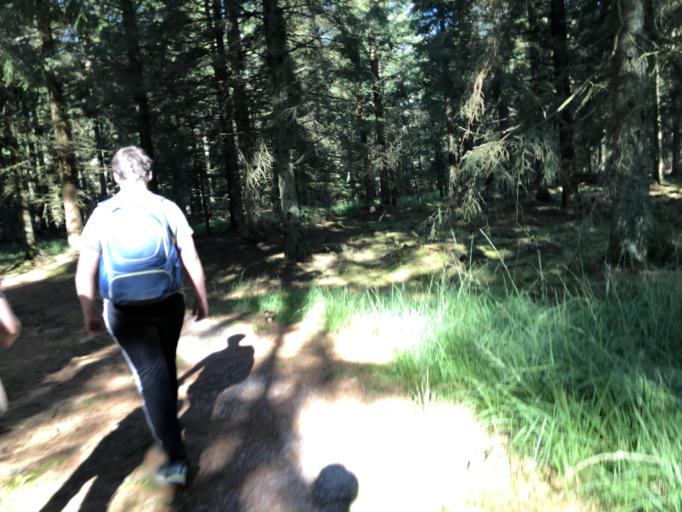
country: DK
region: Central Jutland
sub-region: Lemvig Kommune
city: Lemvig
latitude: 56.4781
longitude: 8.3312
